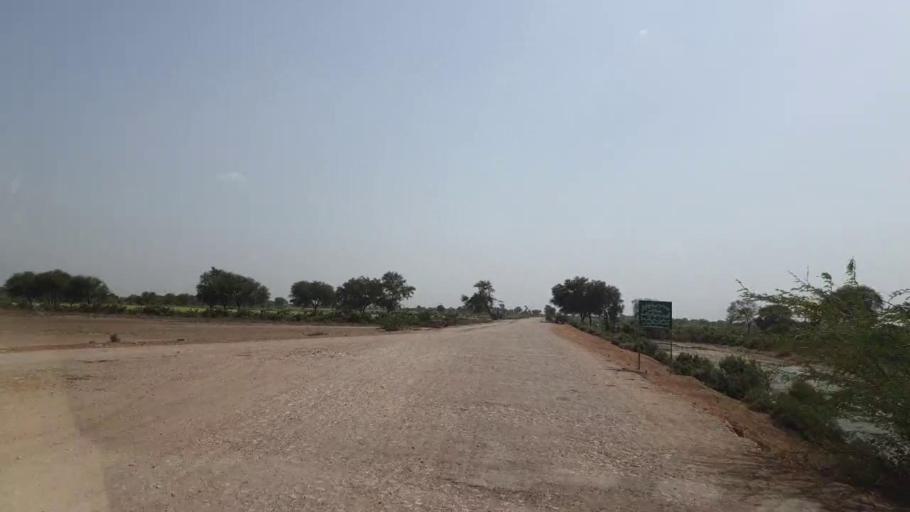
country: PK
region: Sindh
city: Rajo Khanani
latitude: 25.0223
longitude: 68.8730
